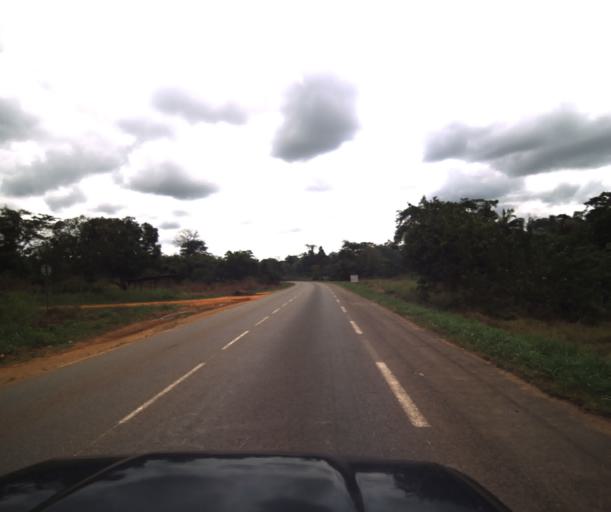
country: CM
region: Littoral
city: Edea
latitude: 3.8474
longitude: 10.4789
